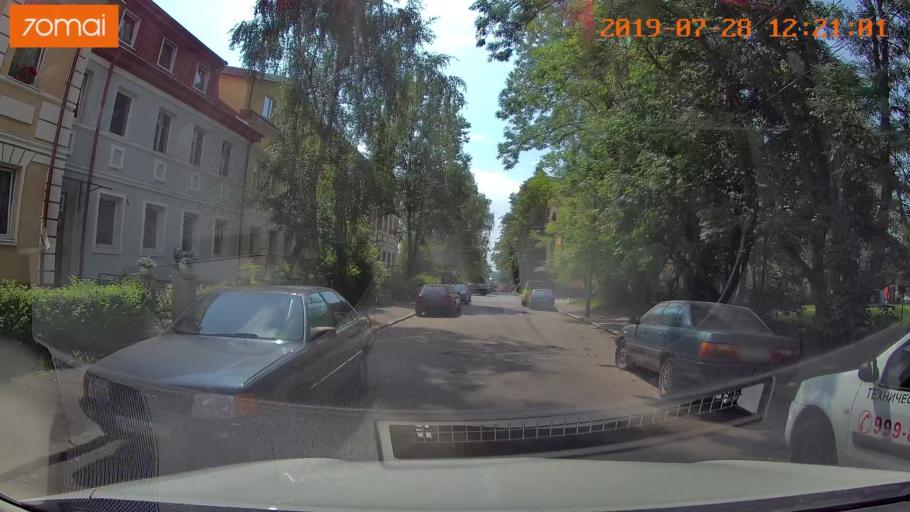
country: RU
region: Kaliningrad
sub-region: Gorod Kaliningrad
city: Kaliningrad
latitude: 54.7126
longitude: 20.4518
